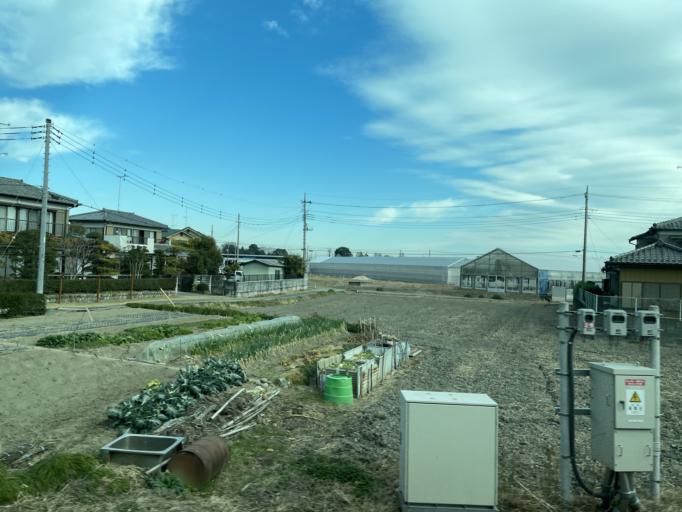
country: JP
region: Saitama
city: Kumagaya
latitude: 36.1220
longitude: 139.4213
